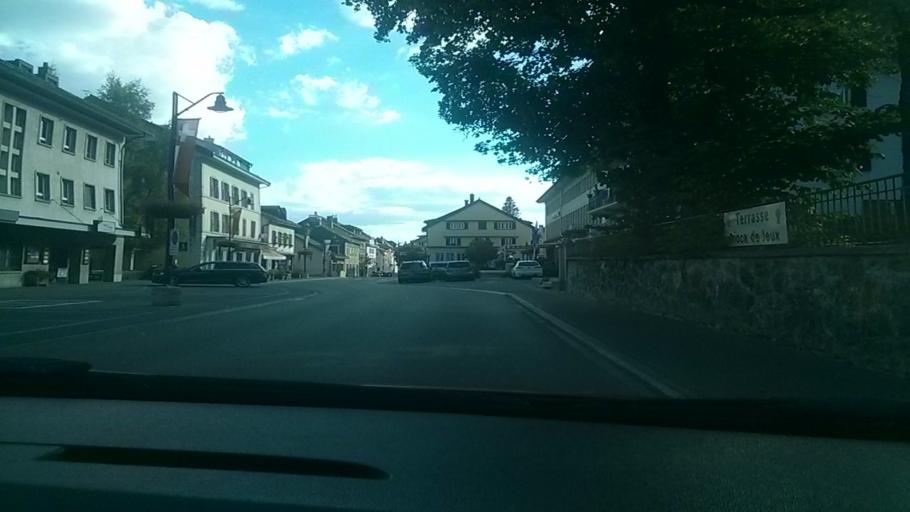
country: CH
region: Vaud
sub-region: Jura-Nord vaudois District
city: Le Chenit
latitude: 46.6080
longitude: 6.2312
